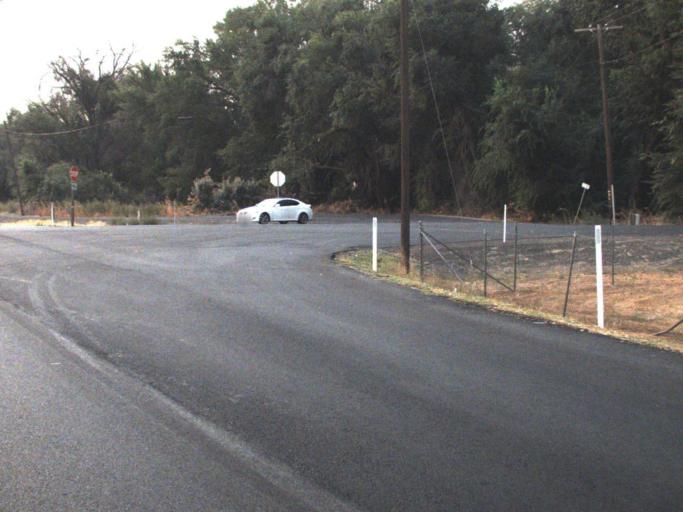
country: US
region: Washington
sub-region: Yakima County
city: Wapato
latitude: 46.4191
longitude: -120.3992
